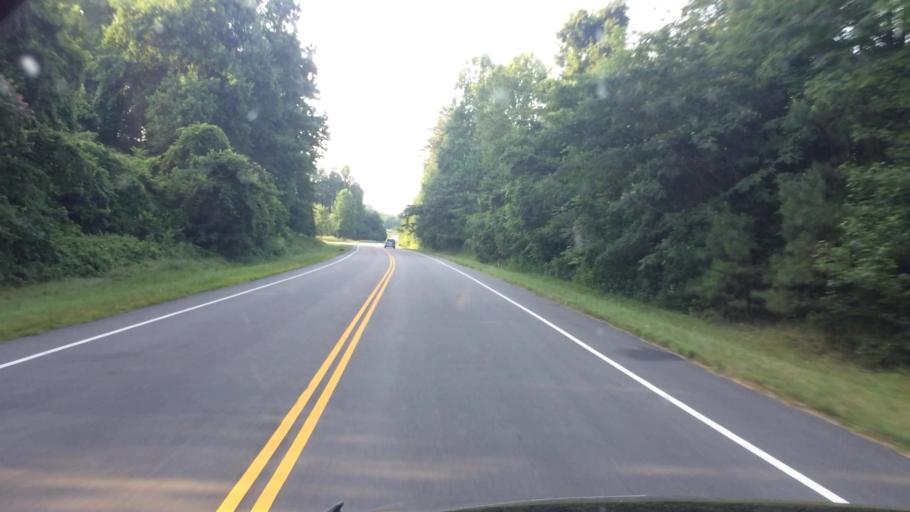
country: US
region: Virginia
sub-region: James City County
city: Williamsburg
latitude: 37.3015
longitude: -76.7266
